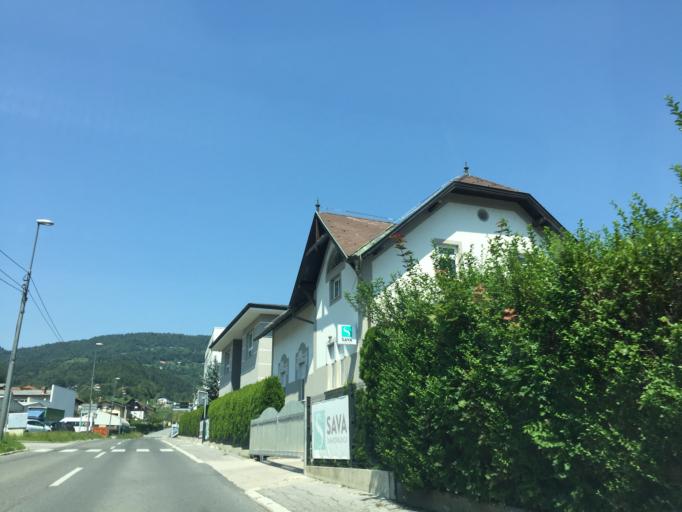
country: SI
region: Trbovlje
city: Trbovlje
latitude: 46.1656
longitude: 15.0517
